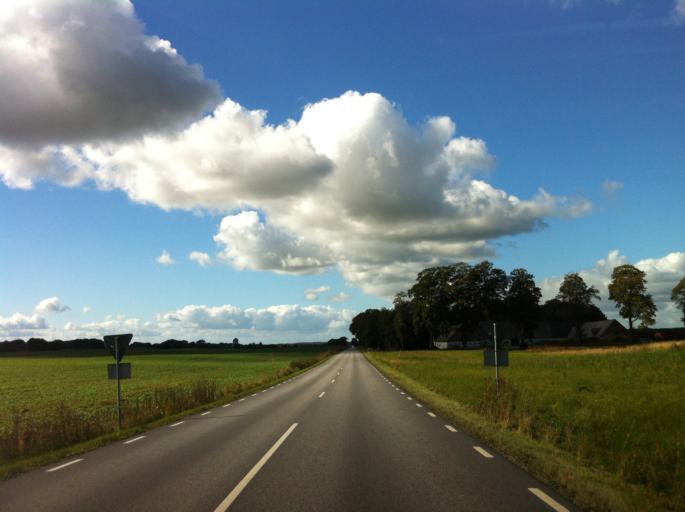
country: SE
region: Skane
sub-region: Tomelilla Kommun
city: Tomelilla
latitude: 55.6420
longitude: 14.0026
